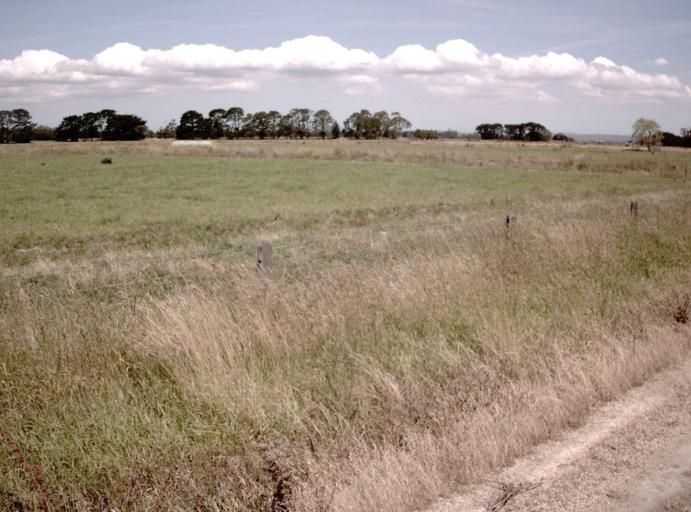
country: AU
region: Victoria
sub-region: Wellington
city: Heyfield
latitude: -38.0597
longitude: 146.8730
